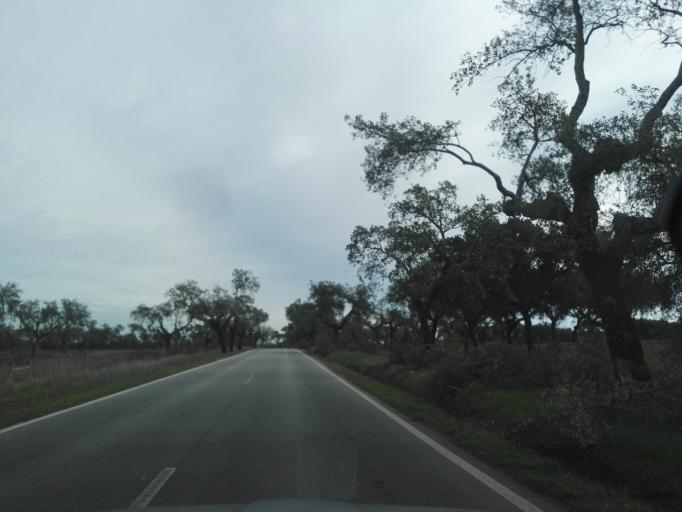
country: PT
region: Portalegre
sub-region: Elvas
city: Elvas
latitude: 38.9358
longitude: -7.1912
